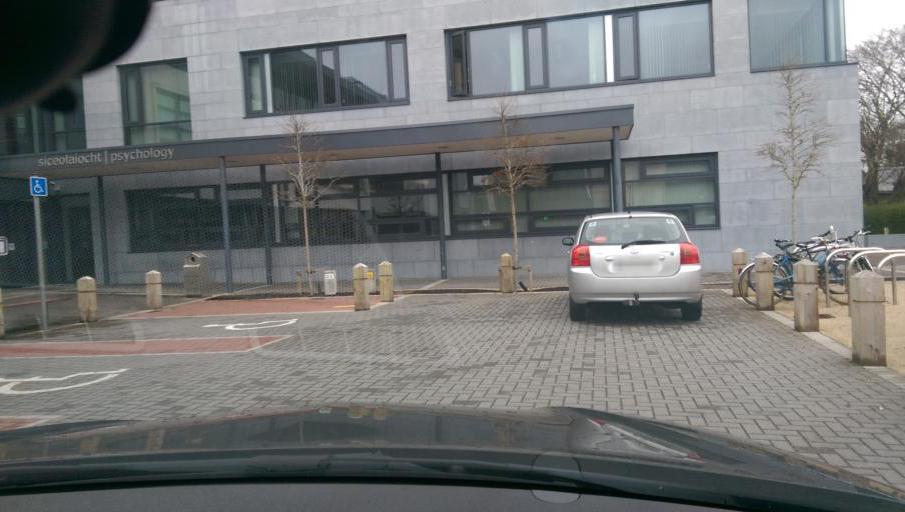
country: IE
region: Connaught
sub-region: County Galway
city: Gaillimh
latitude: 53.2799
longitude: -9.0618
